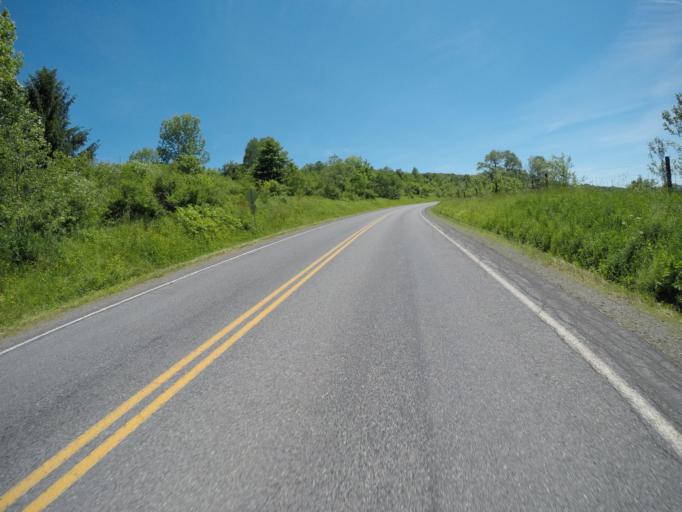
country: US
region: New York
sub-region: Delaware County
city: Delhi
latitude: 42.1956
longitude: -74.8131
